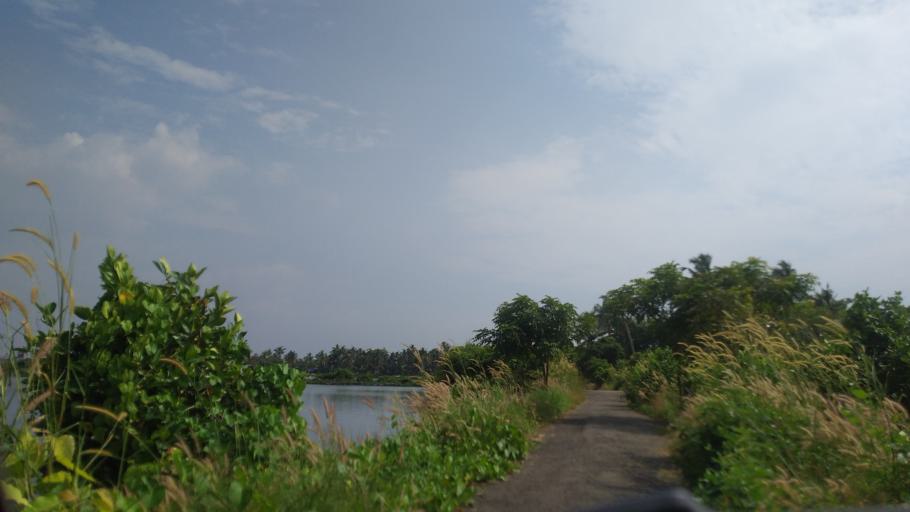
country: IN
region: Kerala
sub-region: Ernakulam
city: Elur
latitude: 10.0855
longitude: 76.2186
